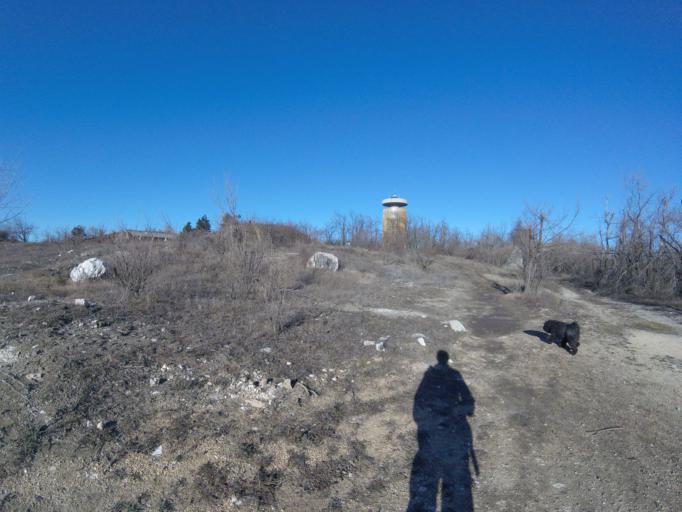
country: HU
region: Pest
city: Pilisszanto
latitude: 47.6878
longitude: 18.8729
